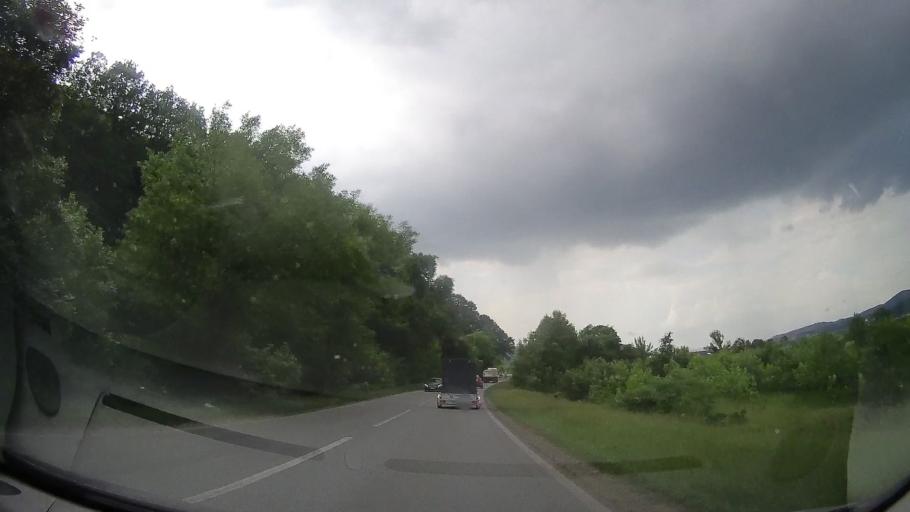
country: RO
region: Hunedoara
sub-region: Comuna Dobra
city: Dobra
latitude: 45.9117
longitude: 22.5204
